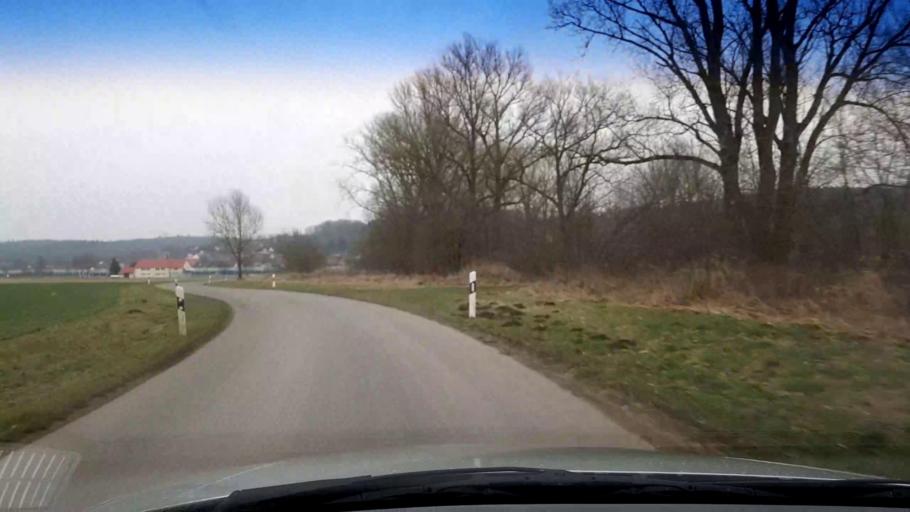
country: DE
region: Bavaria
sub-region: Upper Franconia
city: Zapfendorf
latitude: 50.0373
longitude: 10.9358
